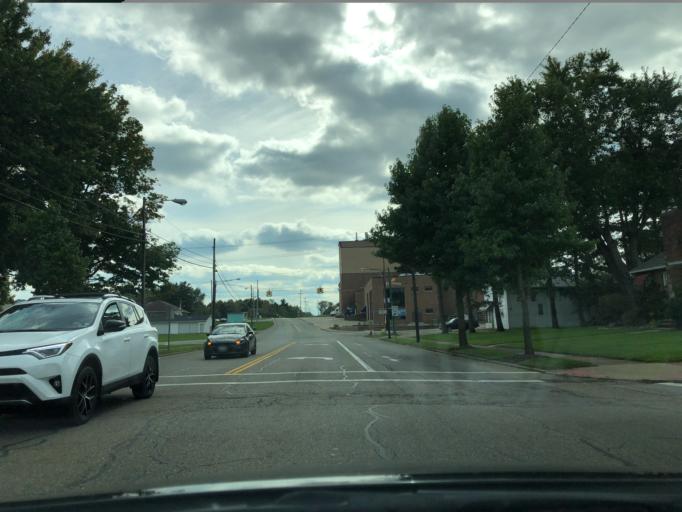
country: US
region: Ohio
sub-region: Stark County
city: Brewster
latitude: 40.7078
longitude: -81.5981
